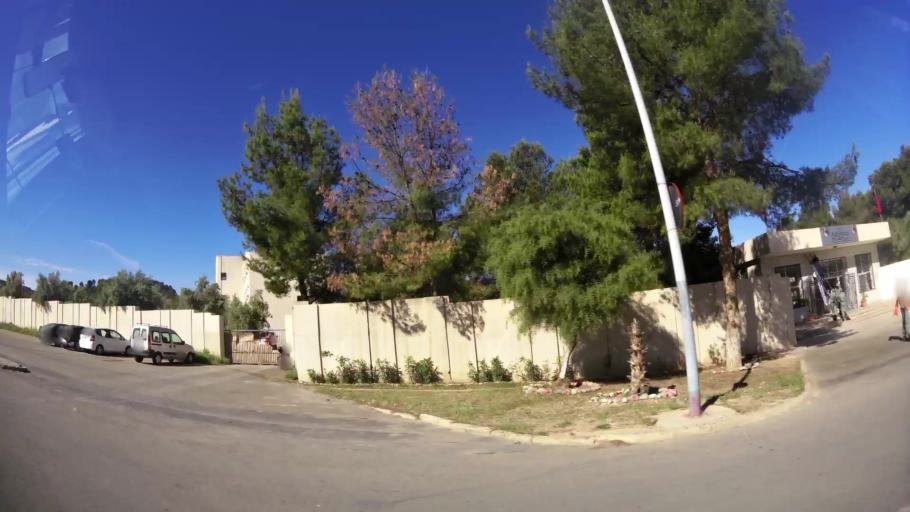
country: MA
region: Oriental
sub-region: Oujda-Angad
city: Oujda
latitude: 34.6505
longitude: -1.8948
